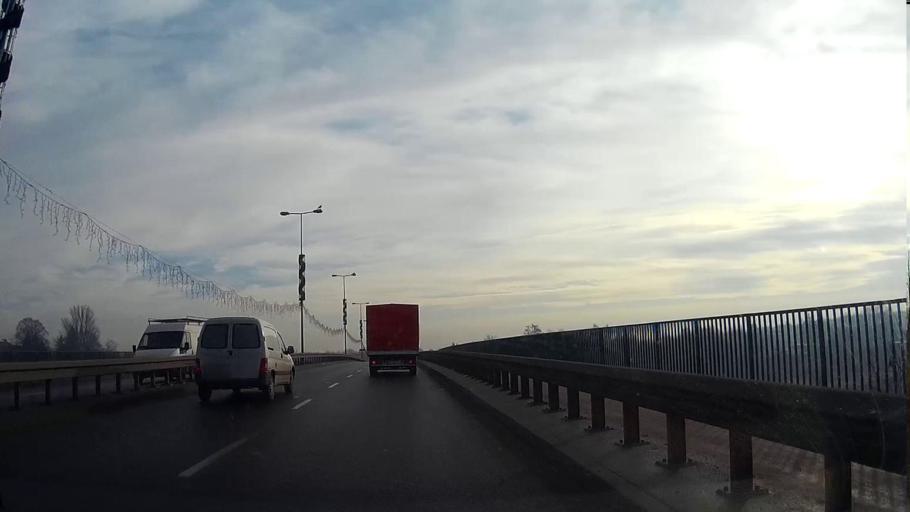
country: PL
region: Lesser Poland Voivodeship
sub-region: Krakow
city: Krakow
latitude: 50.0489
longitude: 19.9056
